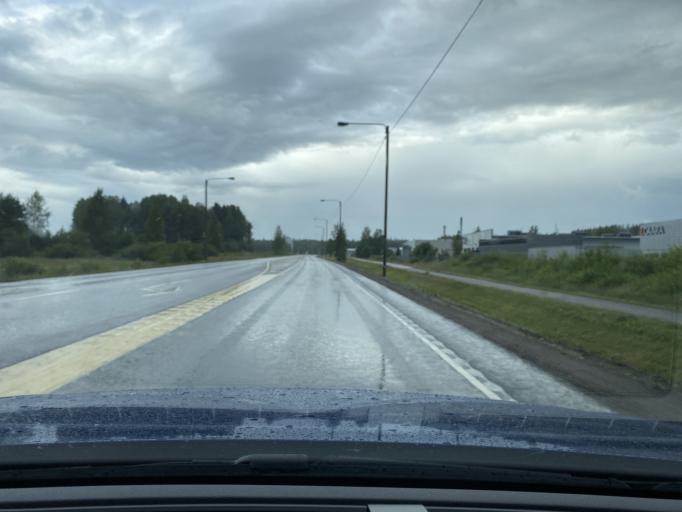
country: FI
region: Uusimaa
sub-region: Helsinki
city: Hyvinge
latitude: 60.6100
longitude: 24.8071
